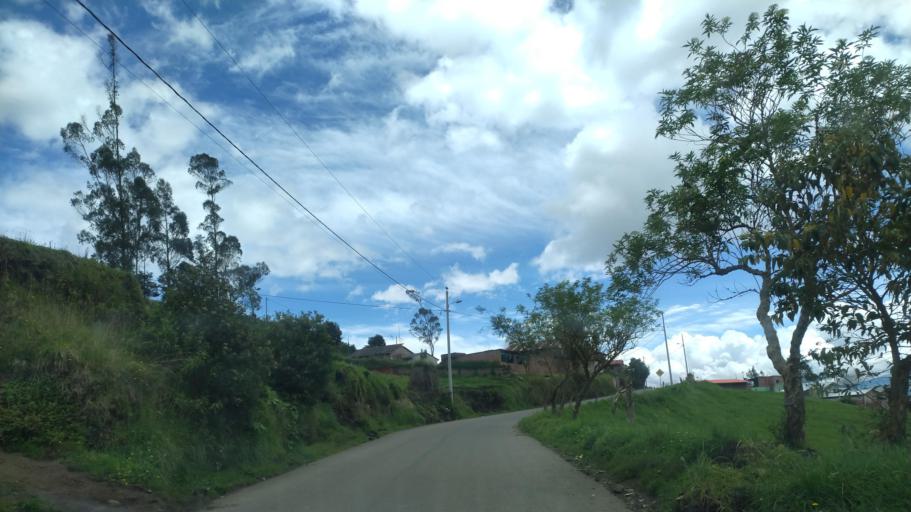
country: EC
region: Chimborazo
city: Riobamba
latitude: -1.6762
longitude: -78.5676
